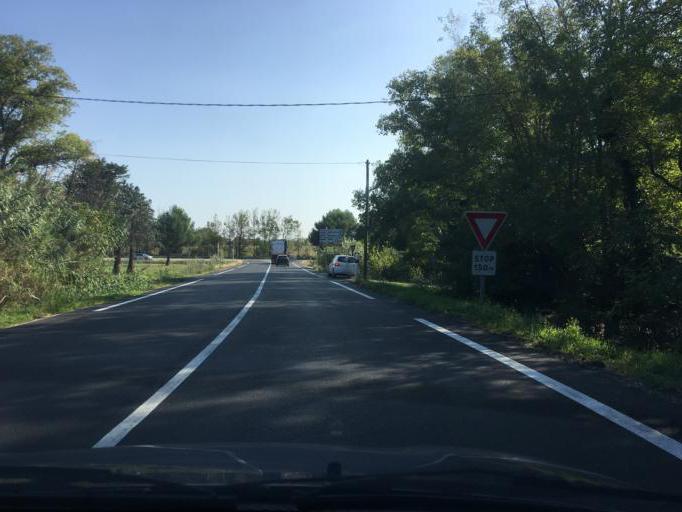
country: FR
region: Languedoc-Roussillon
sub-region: Departement du Gard
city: Villeneuve-les-Avignon
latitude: 43.9483
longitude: 4.7846
